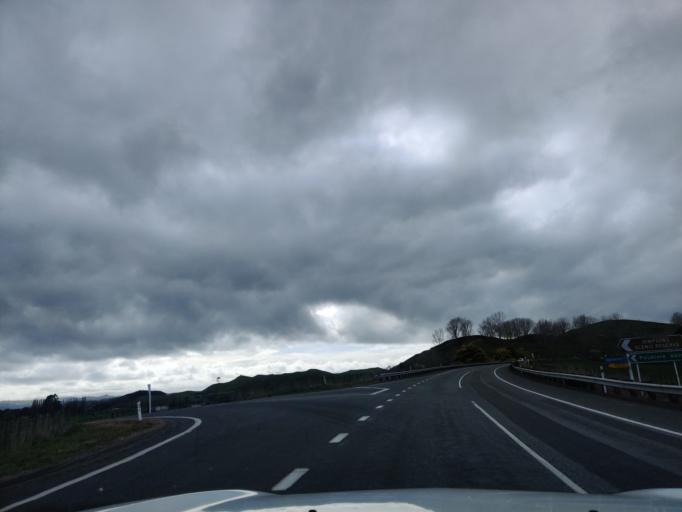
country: NZ
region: Manawatu-Wanganui
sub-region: Rangitikei District
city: Bulls
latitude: -39.9228
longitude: 175.5905
